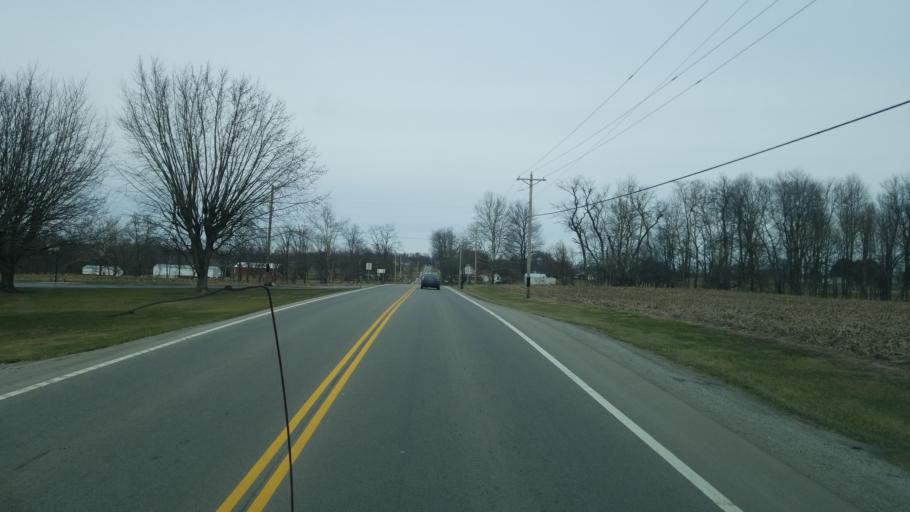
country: US
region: Ohio
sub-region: Highland County
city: Hillsboro
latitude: 39.1385
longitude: -83.6676
